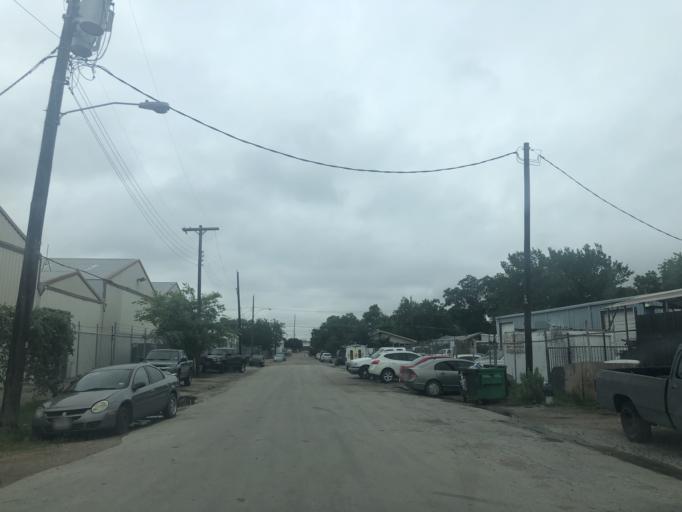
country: US
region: Texas
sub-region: Dallas County
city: Cockrell Hill
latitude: 32.7759
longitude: -96.8576
